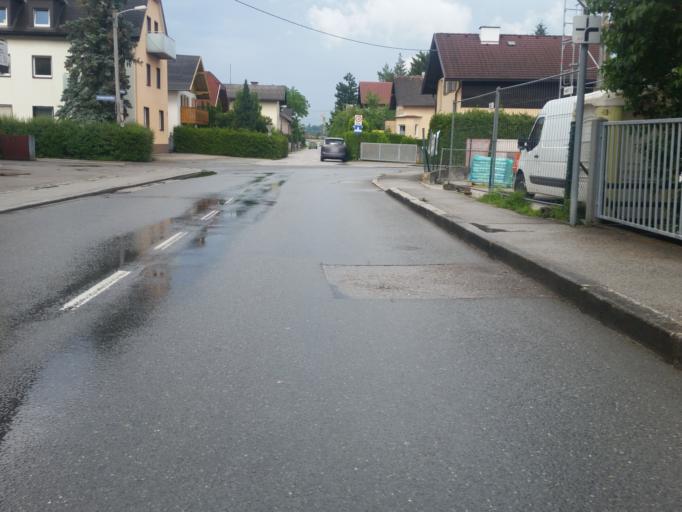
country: AT
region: Salzburg
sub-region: Salzburg Stadt
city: Salzburg
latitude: 47.7801
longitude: 13.0063
